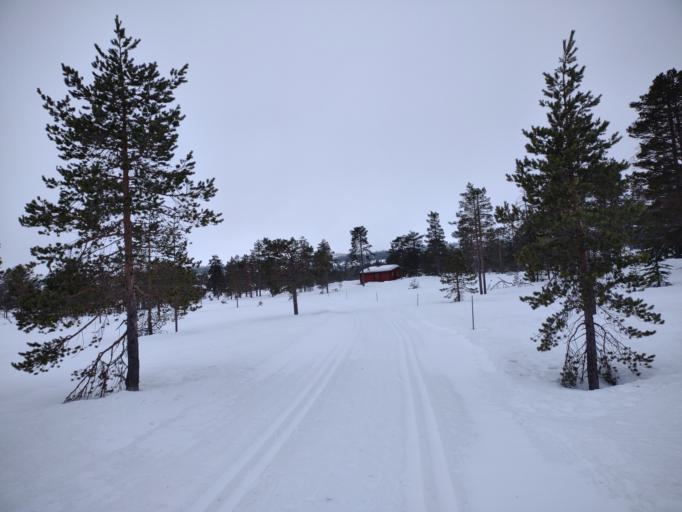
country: NO
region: Buskerud
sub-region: Flesberg
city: Lampeland
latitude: 59.7960
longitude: 9.4343
